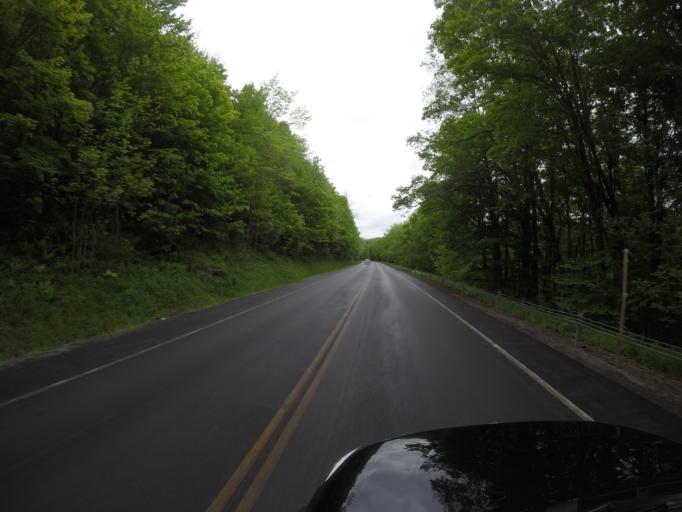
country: US
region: New York
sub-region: Delaware County
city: Delhi
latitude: 42.2302
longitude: -74.7853
